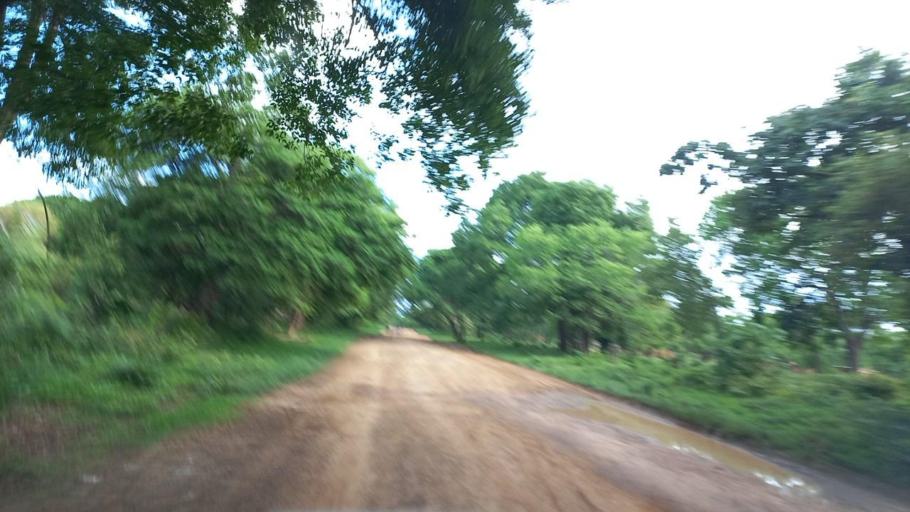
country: ZM
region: North-Western
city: Kabompo
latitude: -13.3730
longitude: 24.2978
